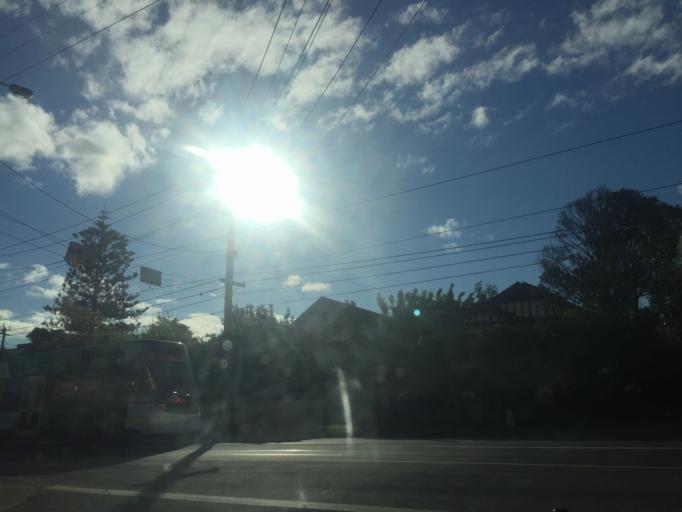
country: AU
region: Victoria
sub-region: Darebin
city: Kingsbury
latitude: -37.7273
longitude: 145.0203
